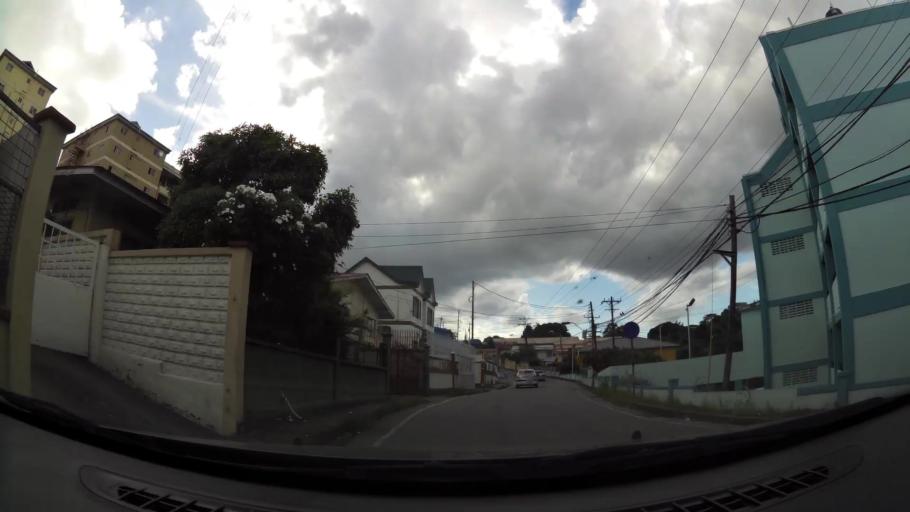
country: TT
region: City of San Fernando
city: San Fernando
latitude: 10.2854
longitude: -61.4561
